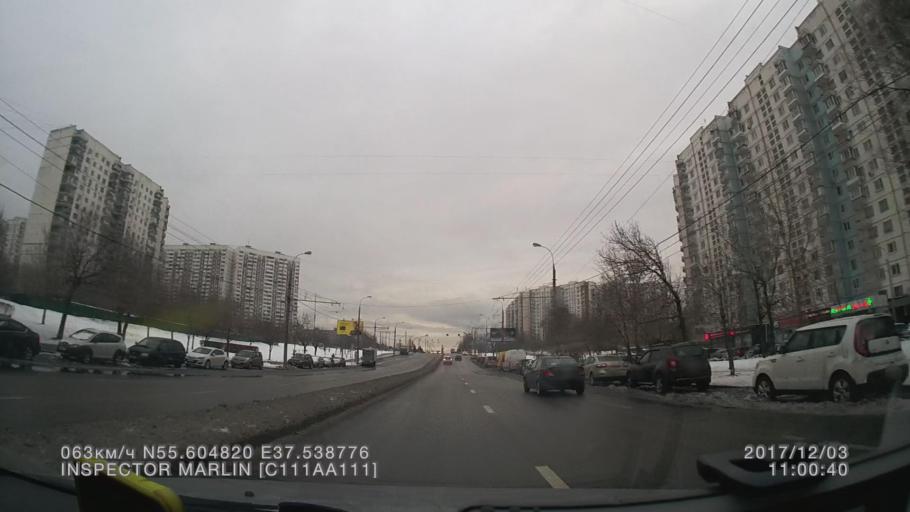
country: RU
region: Moscow
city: Yasenevo
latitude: 55.6048
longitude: 37.5389
